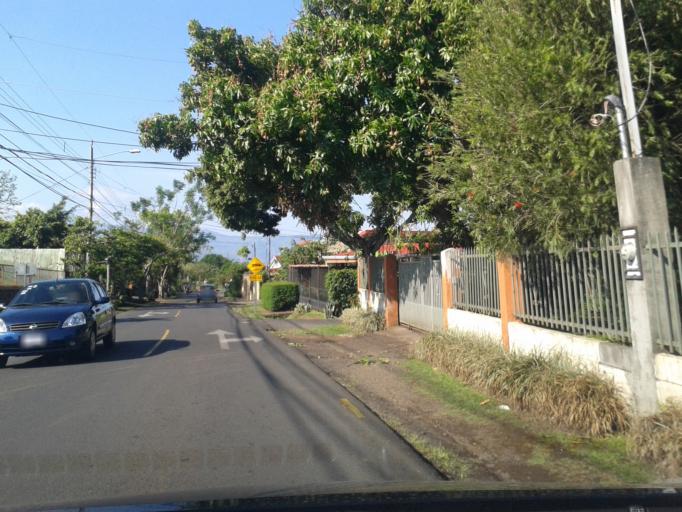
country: CR
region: Heredia
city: Llorente
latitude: 10.0112
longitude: -84.1478
